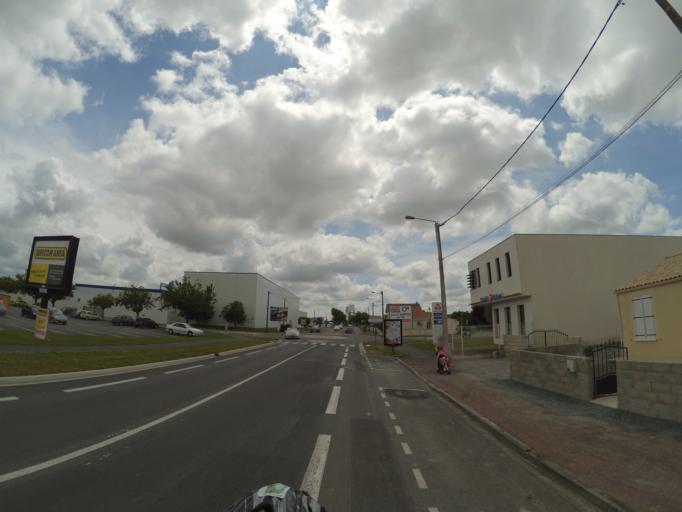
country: FR
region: Poitou-Charentes
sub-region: Departement de la Charente-Maritime
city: Rochefort
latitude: 45.9261
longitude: -0.9600
